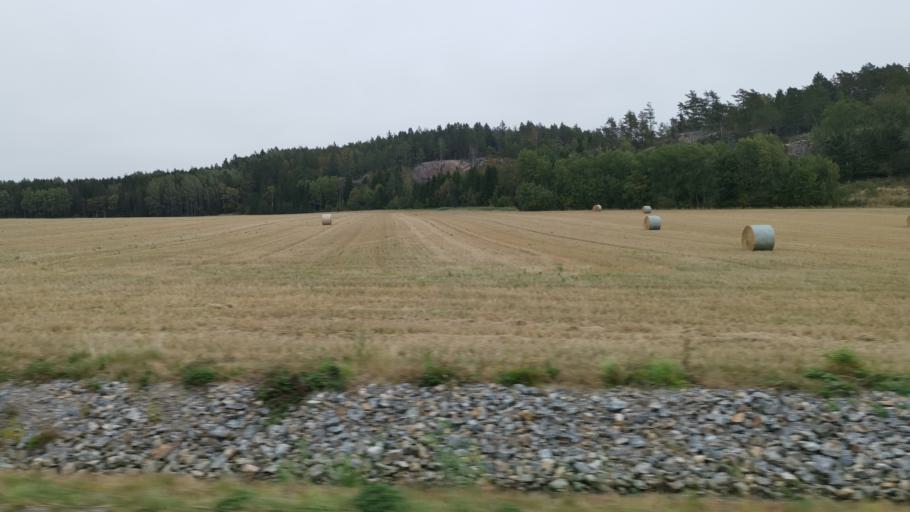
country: SE
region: Vaestra Goetaland
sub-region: Tanums Kommun
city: Tanumshede
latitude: 58.6660
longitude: 11.3444
